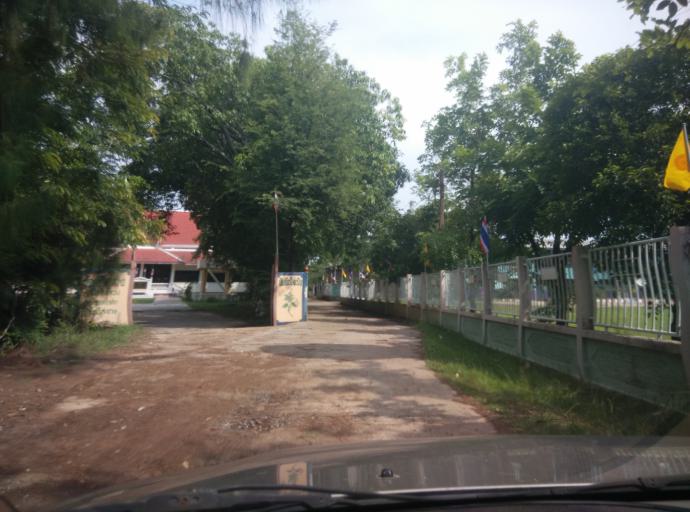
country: TH
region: Sisaket
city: Huai Thap Than
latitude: 15.0512
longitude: 104.0842
